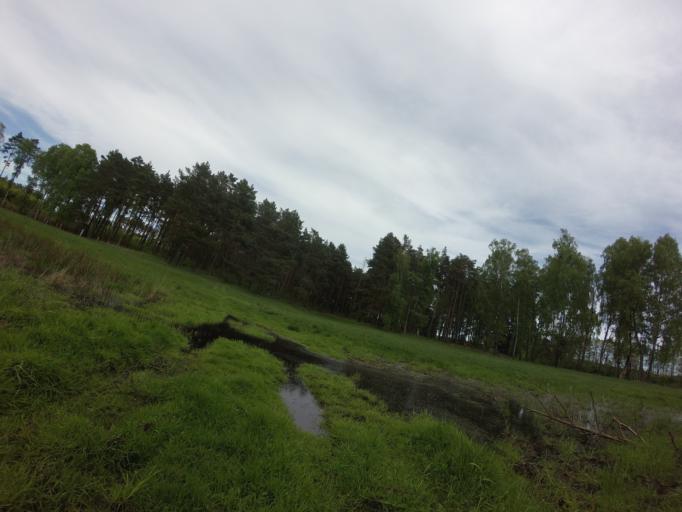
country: PL
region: West Pomeranian Voivodeship
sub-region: Powiat choszczenski
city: Drawno
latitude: 53.1652
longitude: 15.6704
